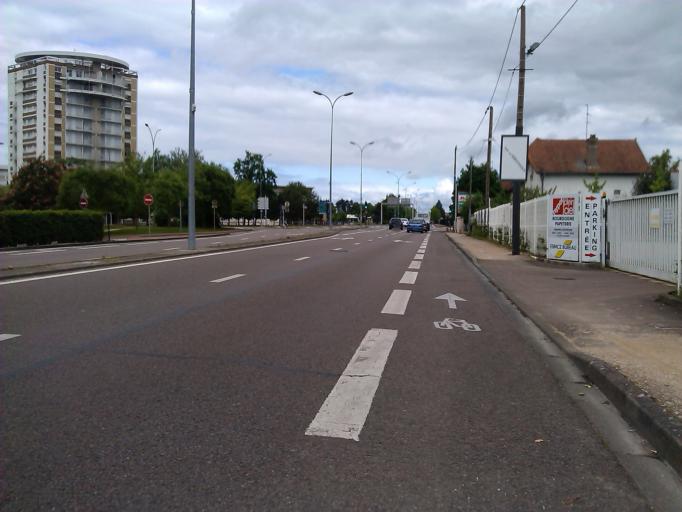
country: FR
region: Bourgogne
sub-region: Departement de Saone-et-Loire
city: Champforgeuil
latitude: 46.8056
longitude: 4.8447
